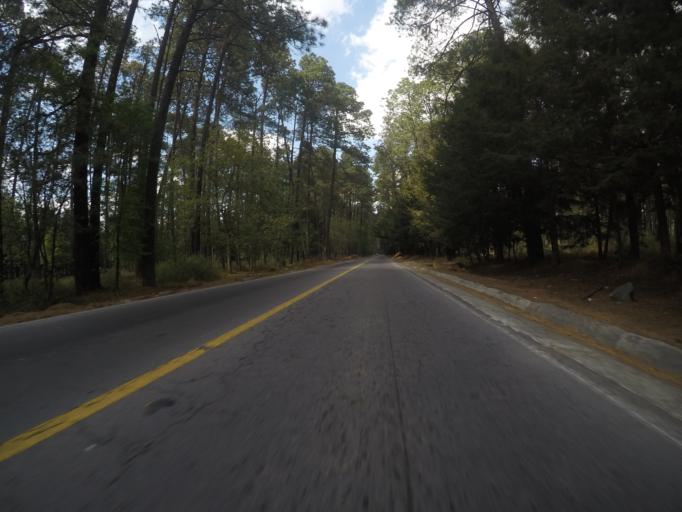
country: MX
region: Mexico
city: Cerro La Calera
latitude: 19.2091
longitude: -99.8088
